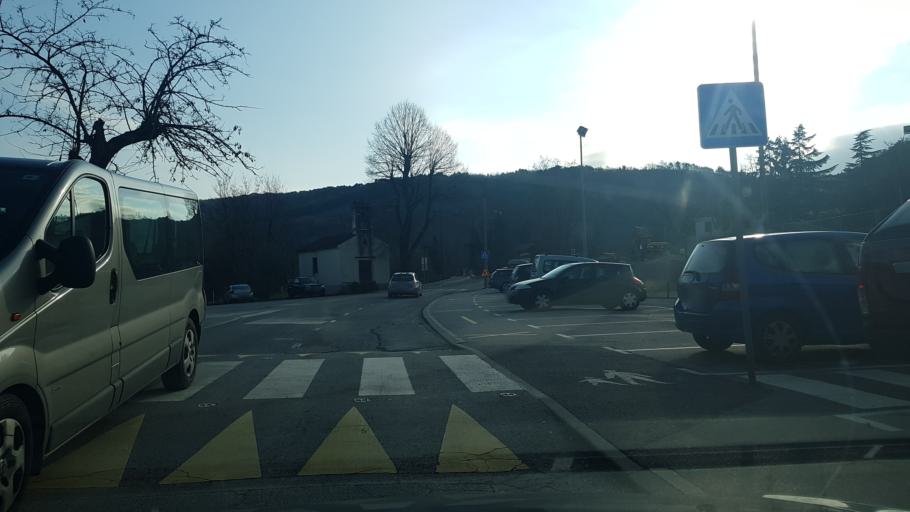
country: SI
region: Koper-Capodistria
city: Prade
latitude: 45.5185
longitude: 13.7783
